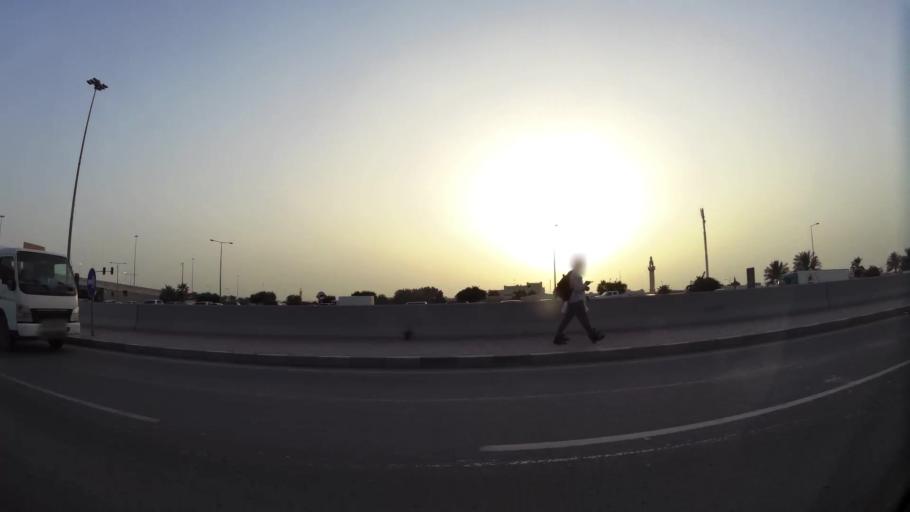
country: QA
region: Baladiyat ar Rayyan
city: Ar Rayyan
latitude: 25.2267
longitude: 51.4318
